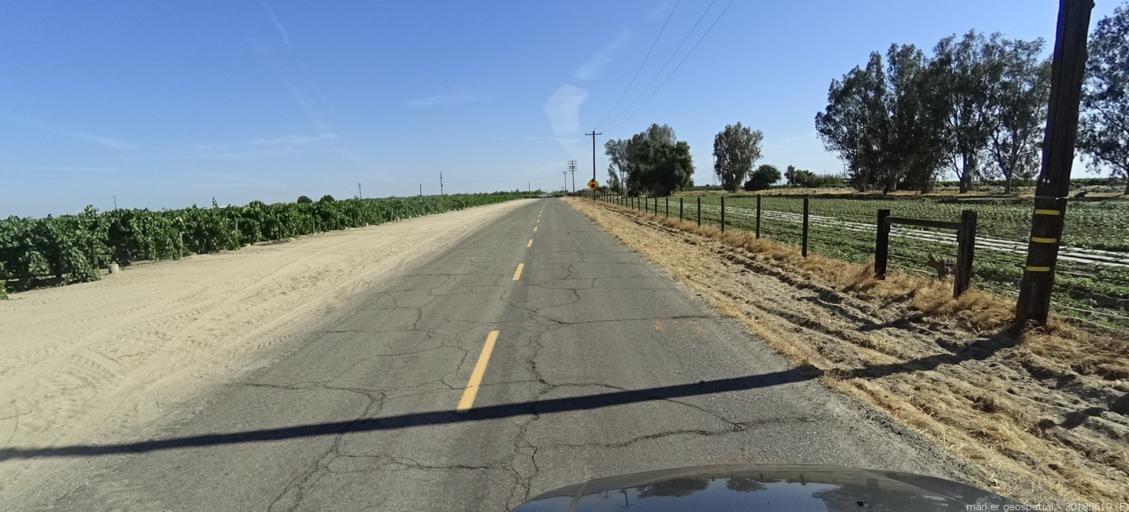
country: US
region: California
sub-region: Fresno County
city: Biola
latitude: 36.8272
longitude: -120.0574
